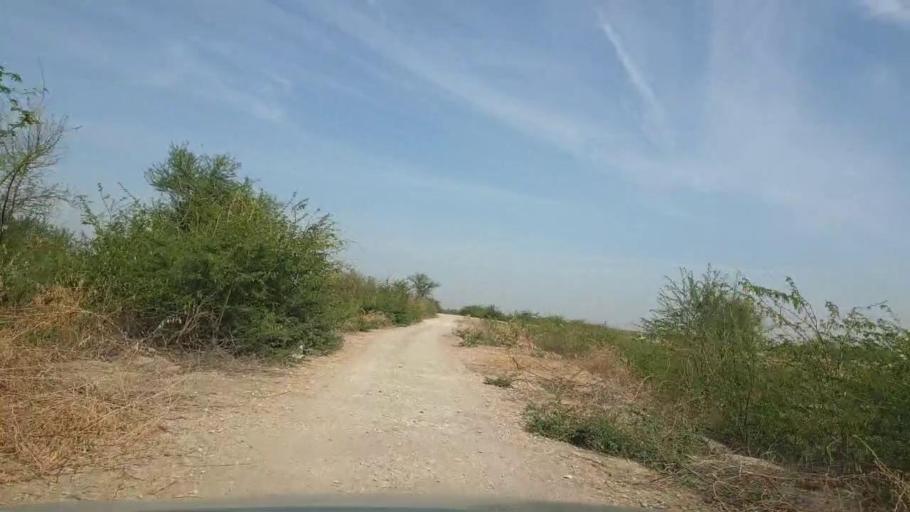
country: PK
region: Sindh
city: Nabisar
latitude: 25.1261
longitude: 69.6393
